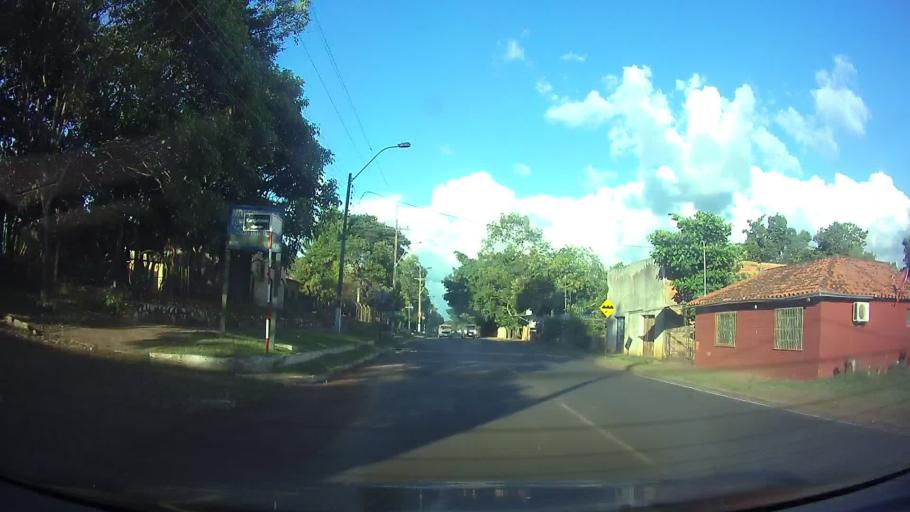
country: PY
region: Cordillera
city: Emboscada
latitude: -25.1902
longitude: -57.3079
